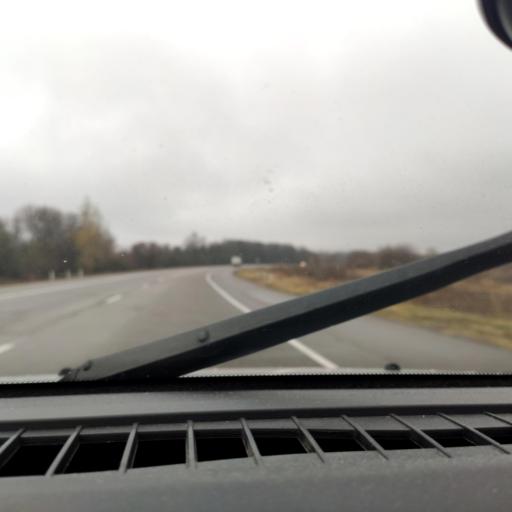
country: RU
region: Voronezj
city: Kolodeznyy
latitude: 51.3140
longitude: 39.0297
